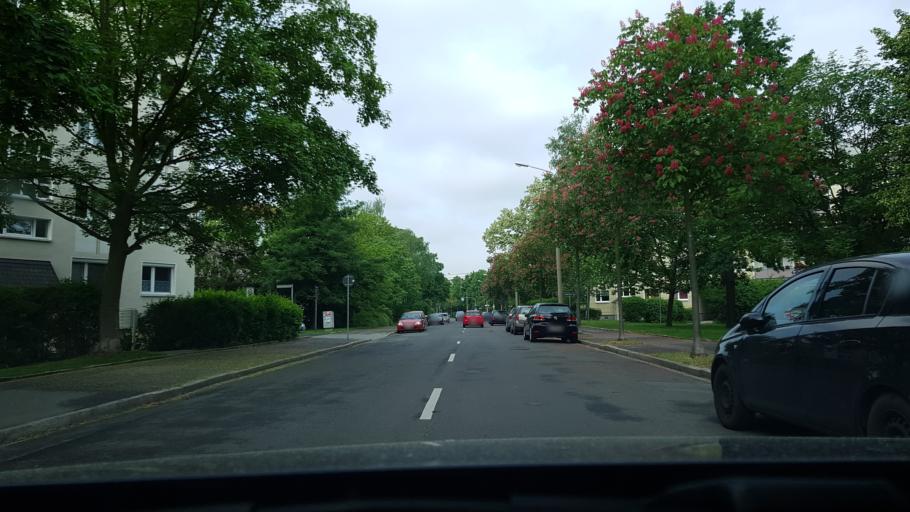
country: DE
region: Saxony
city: Heidenau
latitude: 51.0110
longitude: 13.8196
